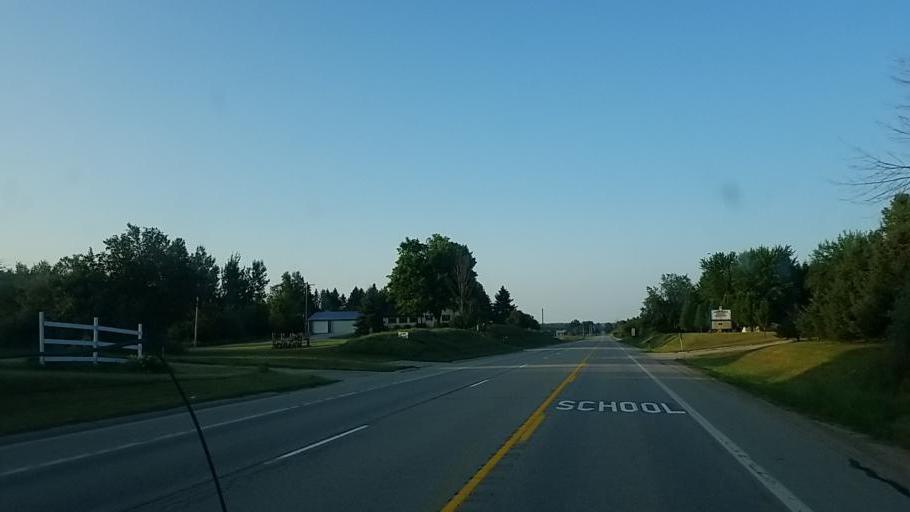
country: US
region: Michigan
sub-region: Isabella County
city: Lake Isabella
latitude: 43.6699
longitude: -85.1464
